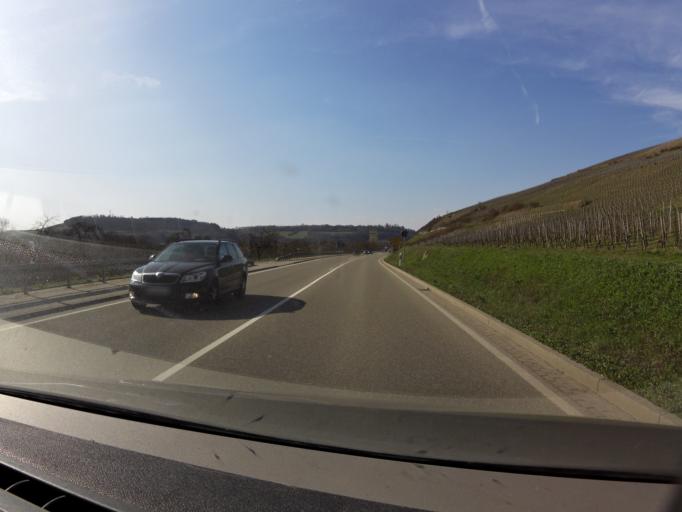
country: DE
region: Baden-Wuerttemberg
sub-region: Regierungsbezirk Stuttgart
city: Igersheim
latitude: 49.4764
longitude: 9.8413
